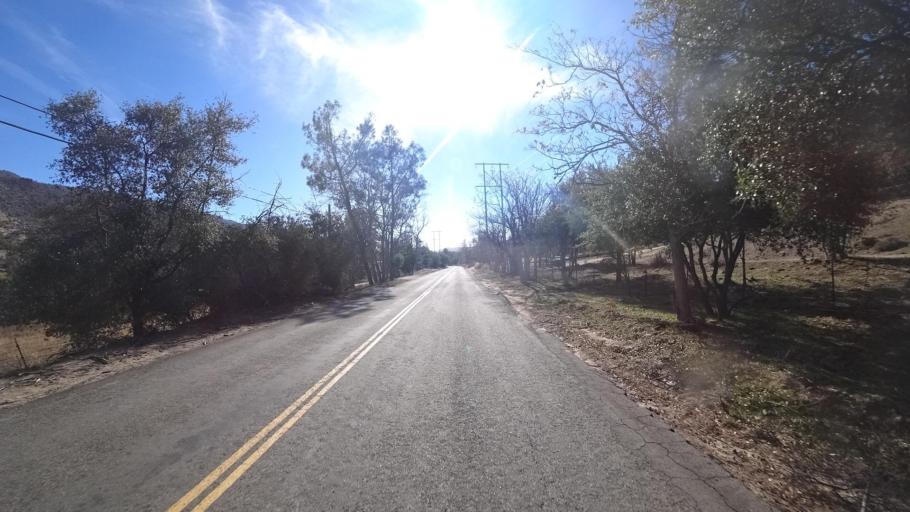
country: US
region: California
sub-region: Kern County
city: Bodfish
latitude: 35.5016
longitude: -118.5222
